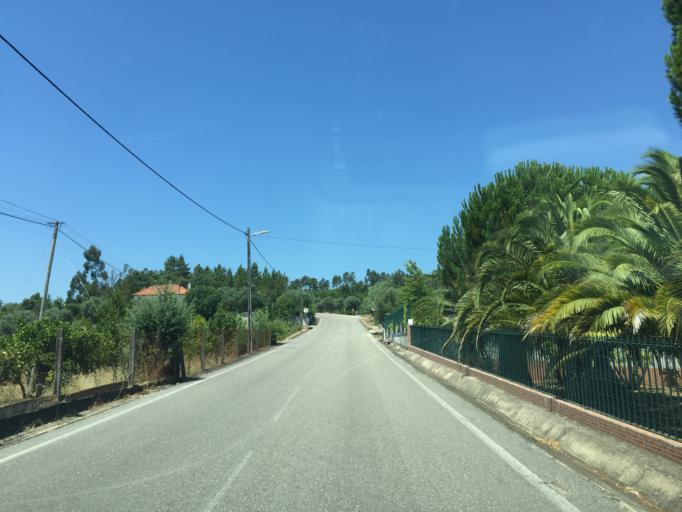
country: PT
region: Santarem
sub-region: Ferreira do Zezere
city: Ferreira do Zezere
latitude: 39.5958
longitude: -8.2848
